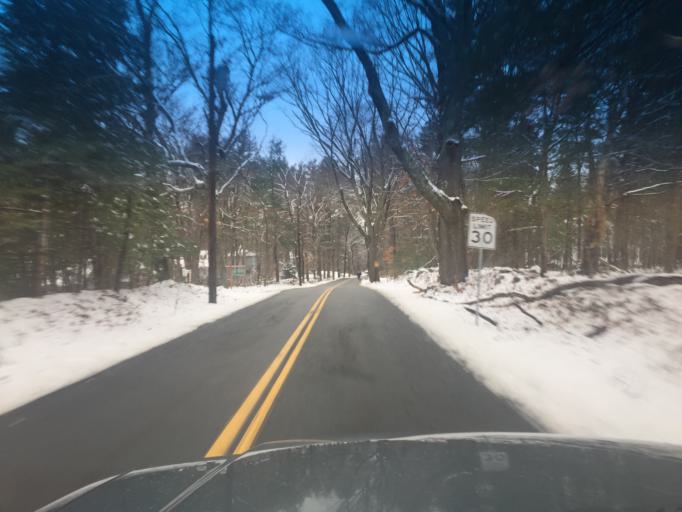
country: US
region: Massachusetts
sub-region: Middlesex County
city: Holliston
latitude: 42.1997
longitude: -71.3927
